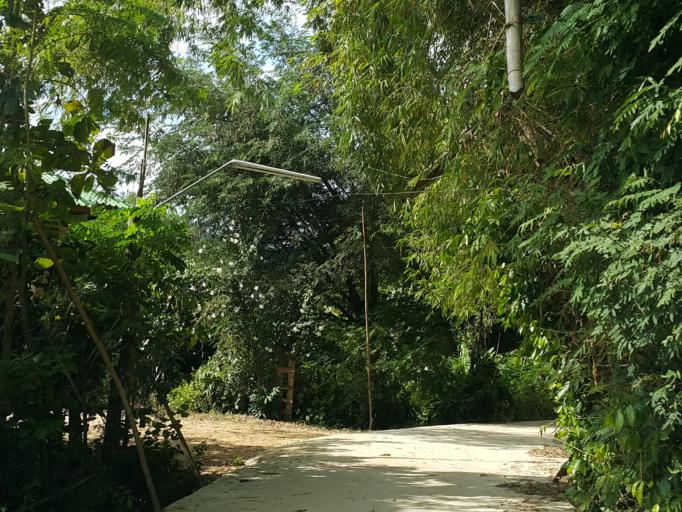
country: TH
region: Lampang
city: Chae Hom
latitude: 18.5643
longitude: 99.4521
